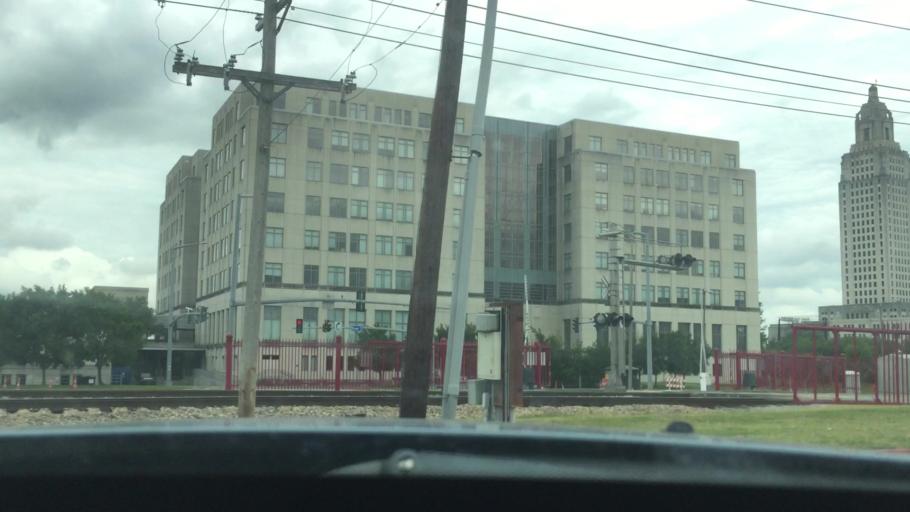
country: US
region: Louisiana
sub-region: West Baton Rouge Parish
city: Port Allen
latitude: 30.4605
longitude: -91.1901
